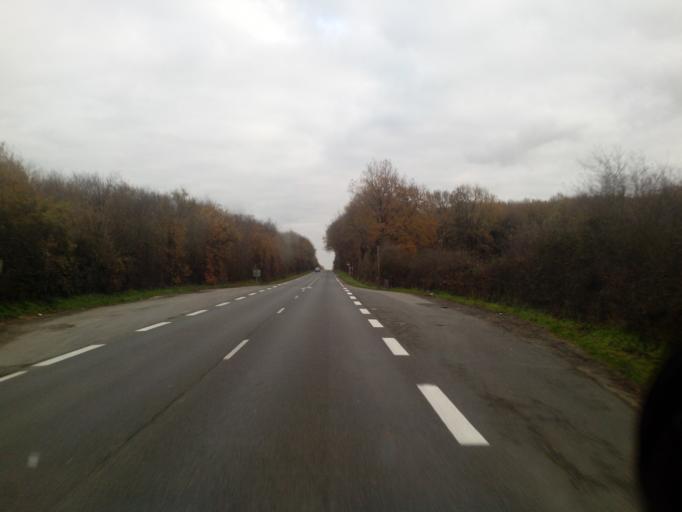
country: FR
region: Poitou-Charentes
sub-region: Departement des Deux-Sevres
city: Chiche
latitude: 46.8127
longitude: -0.3925
